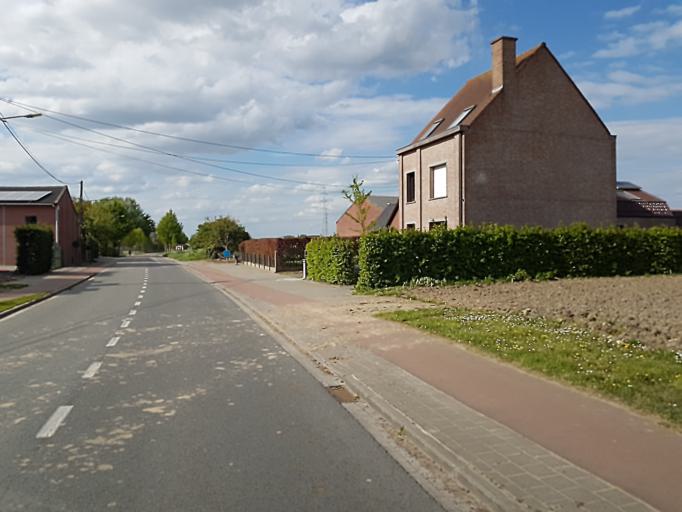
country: BE
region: Flanders
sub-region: Provincie West-Vlaanderen
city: Avelgem
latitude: 50.7908
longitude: 3.4419
